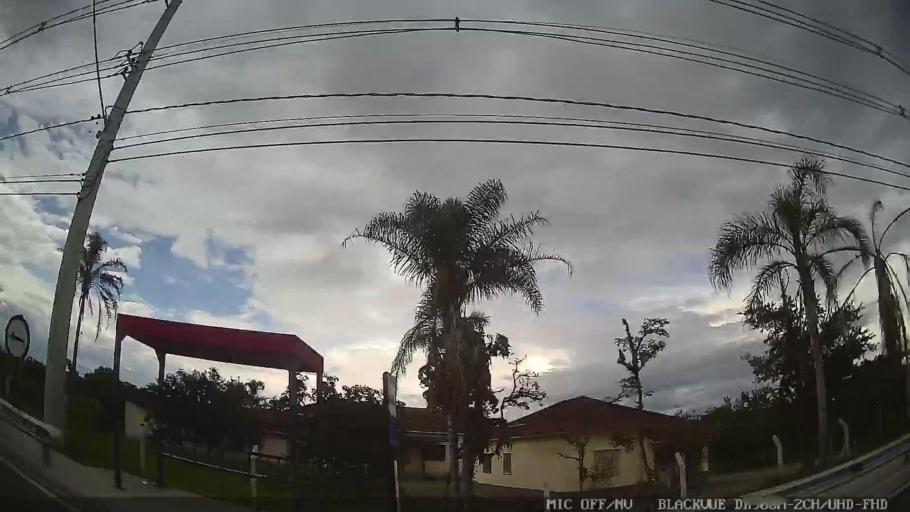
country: BR
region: Sao Paulo
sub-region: Biritiba-Mirim
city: Biritiba Mirim
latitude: -23.5682
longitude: -46.0508
